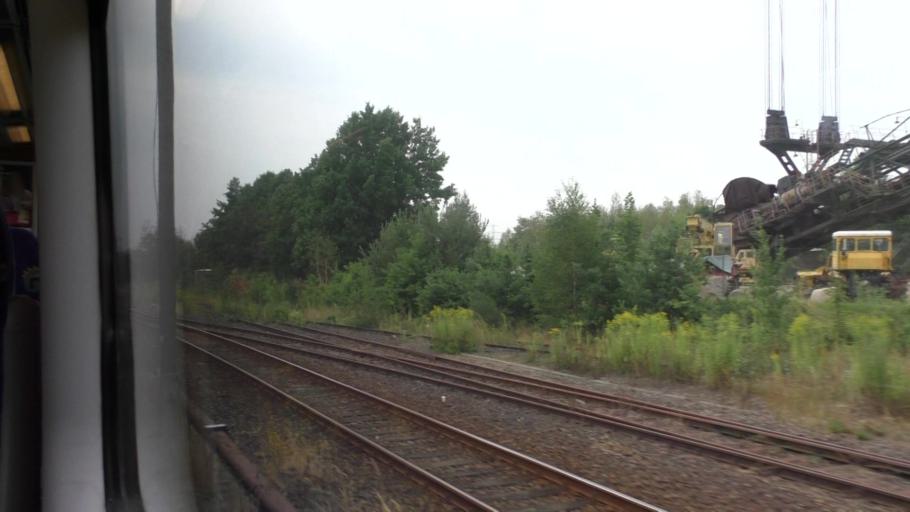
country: DE
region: Saxony
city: Ostritz
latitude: 51.0676
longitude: 14.9588
